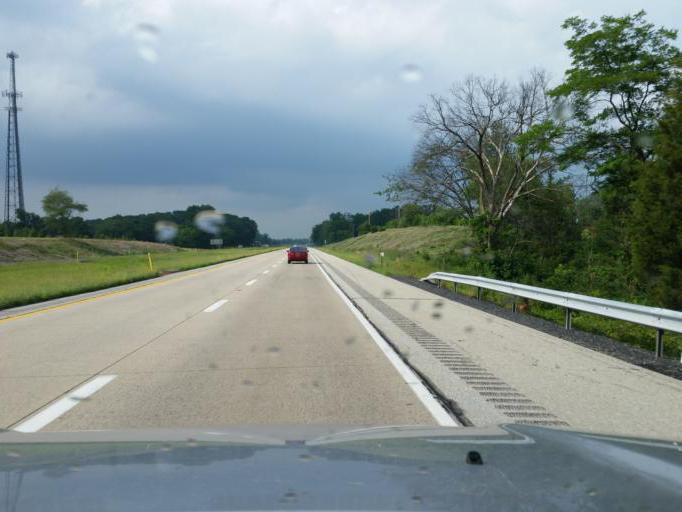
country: US
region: Pennsylvania
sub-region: Adams County
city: Gettysburg
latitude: 39.8777
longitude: -77.1890
